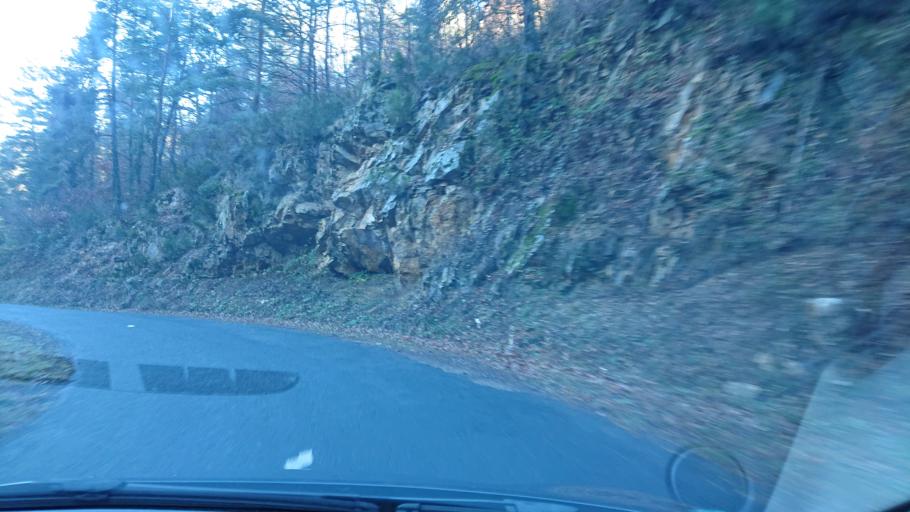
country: FR
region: Auvergne
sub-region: Departement de la Haute-Loire
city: Vorey
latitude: 45.2151
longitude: 3.9254
